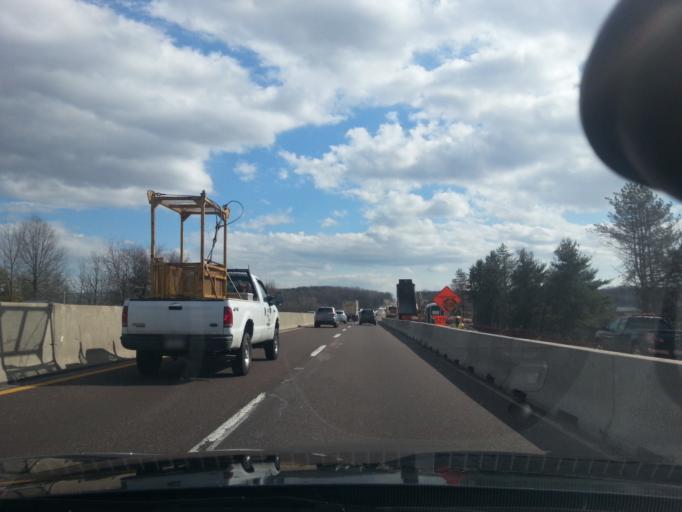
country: US
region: Pennsylvania
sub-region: Montgomery County
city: Kulpsville
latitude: 40.2044
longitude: -75.3204
